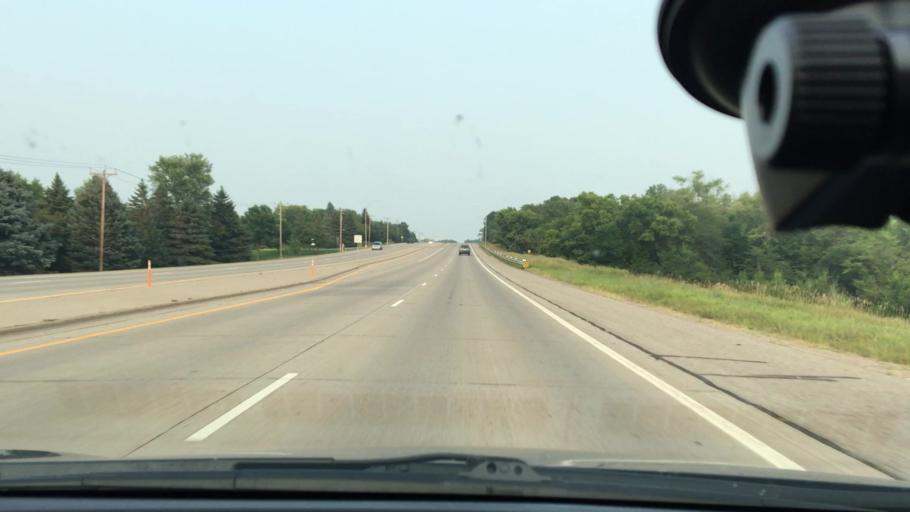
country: US
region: Minnesota
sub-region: Wright County
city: Albertville
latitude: 45.2136
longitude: -93.6134
